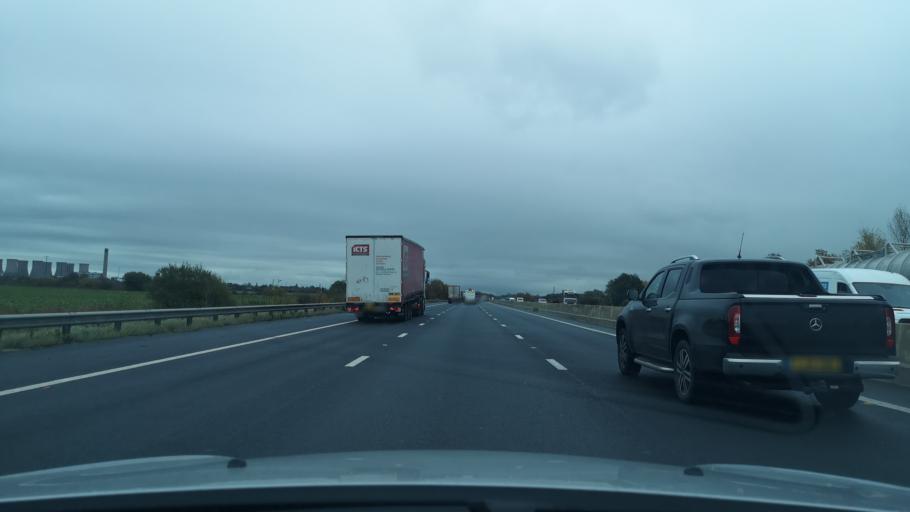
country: GB
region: England
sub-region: Doncaster
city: Norton
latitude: 53.6954
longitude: -1.1857
